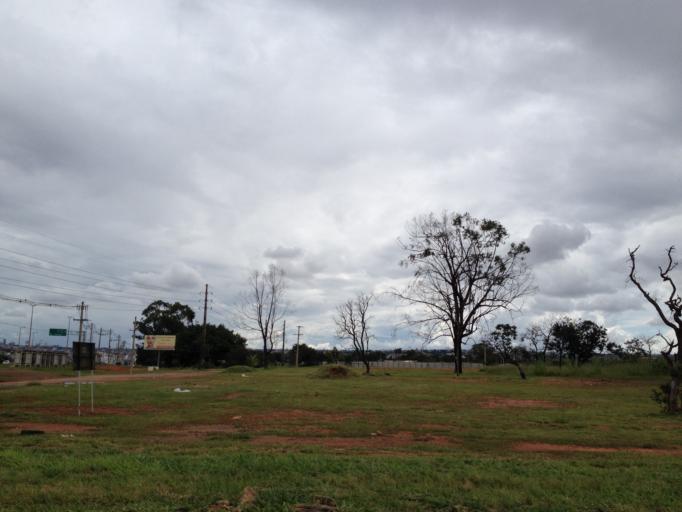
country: BR
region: Federal District
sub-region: Brasilia
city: Brasilia
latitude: -15.8100
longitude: -47.9928
